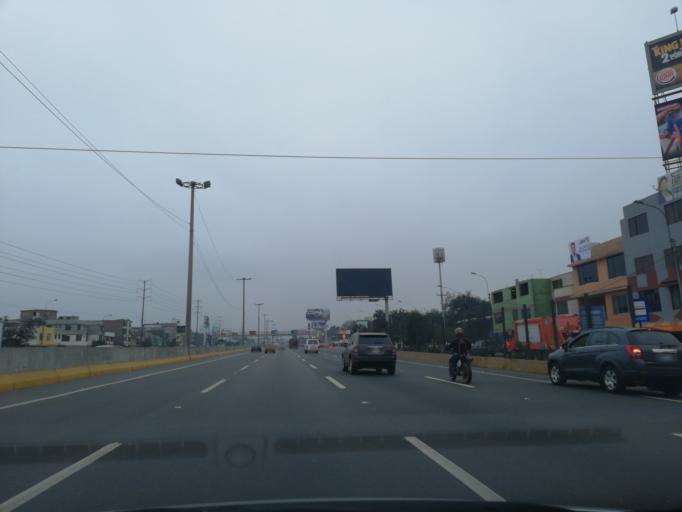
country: PE
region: Lima
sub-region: Lima
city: San Luis
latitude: -12.0761
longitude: -76.9750
